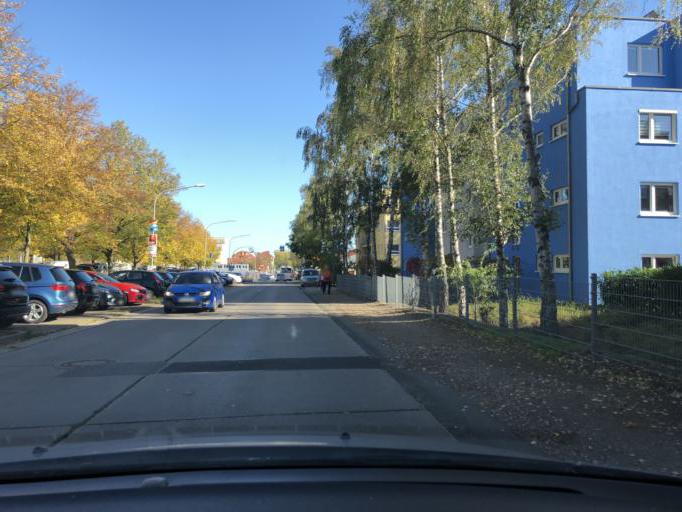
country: DE
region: Thuringia
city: Weimar
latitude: 50.9940
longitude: 11.3128
